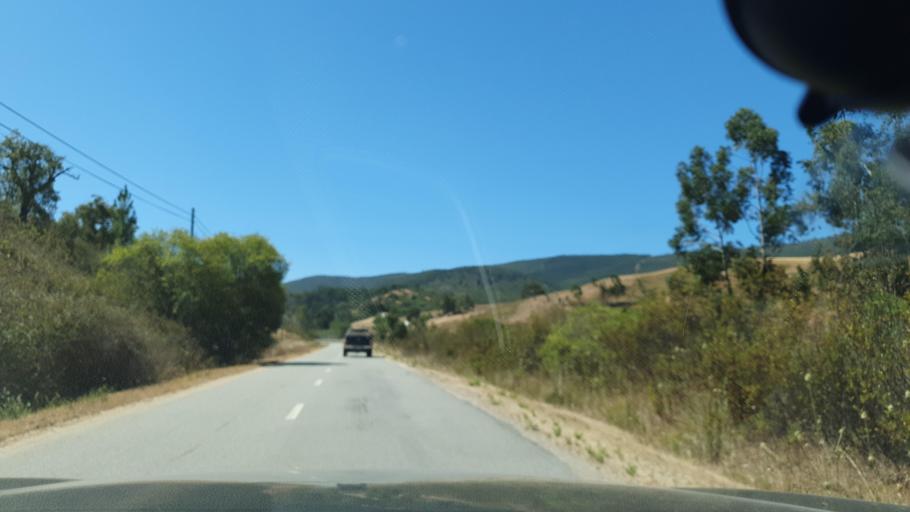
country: PT
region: Faro
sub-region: Monchique
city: Monchique
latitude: 37.4285
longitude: -8.5553
